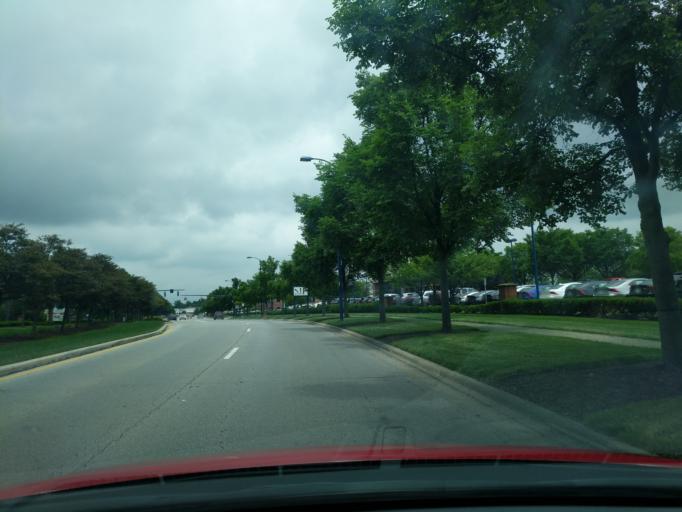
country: US
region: Ohio
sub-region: Franklin County
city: Minerva Park
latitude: 40.0541
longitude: -82.9185
